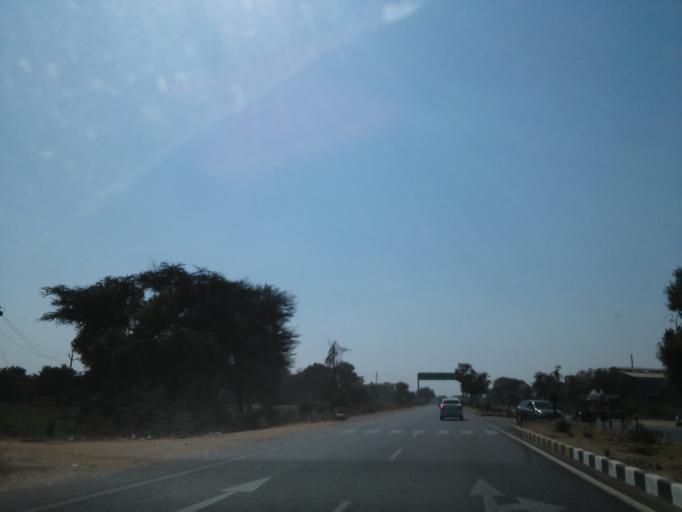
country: IN
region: Gujarat
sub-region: Gandhinagar
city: Chhala
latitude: 23.3692
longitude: 72.8014
